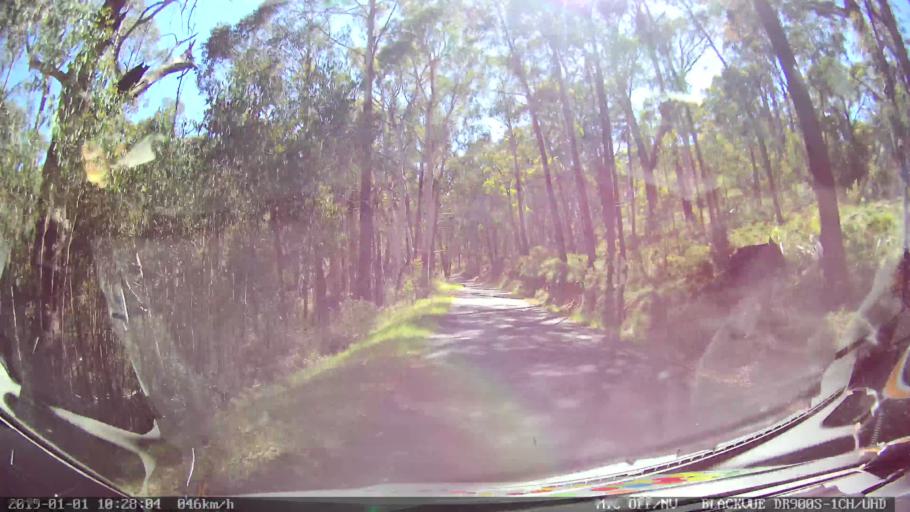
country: AU
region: New South Wales
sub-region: Snowy River
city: Jindabyne
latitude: -36.0622
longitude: 148.2375
